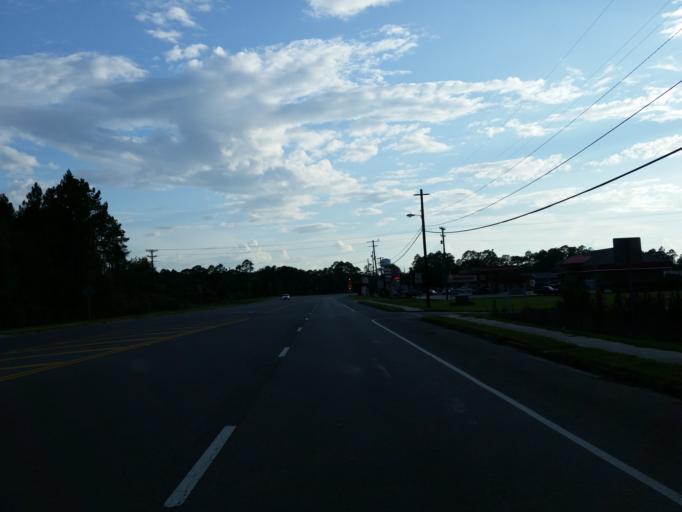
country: US
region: Georgia
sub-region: Clinch County
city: Homerville
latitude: 31.0349
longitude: -82.7594
